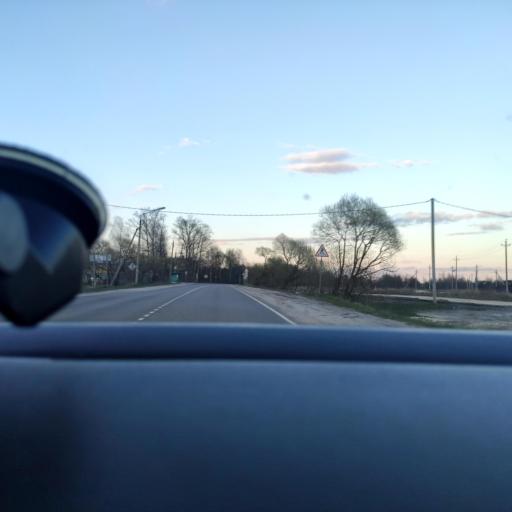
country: RU
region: Moskovskaya
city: Krasnyy Tkach
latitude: 55.4285
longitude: 39.2002
